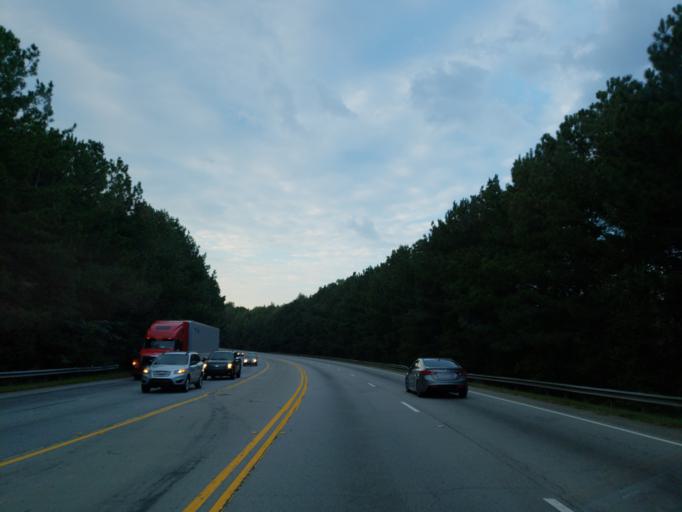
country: US
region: Georgia
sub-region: Cobb County
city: Powder Springs
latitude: 33.8707
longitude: -84.6969
